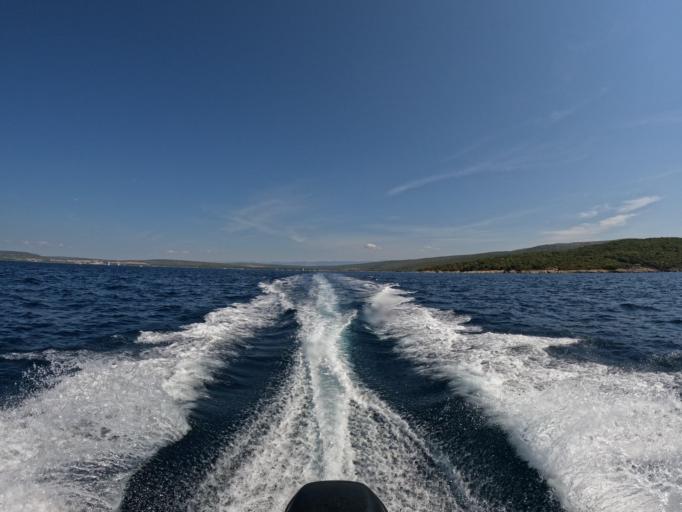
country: HR
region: Primorsko-Goranska
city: Punat
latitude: 44.9777
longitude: 14.6099
